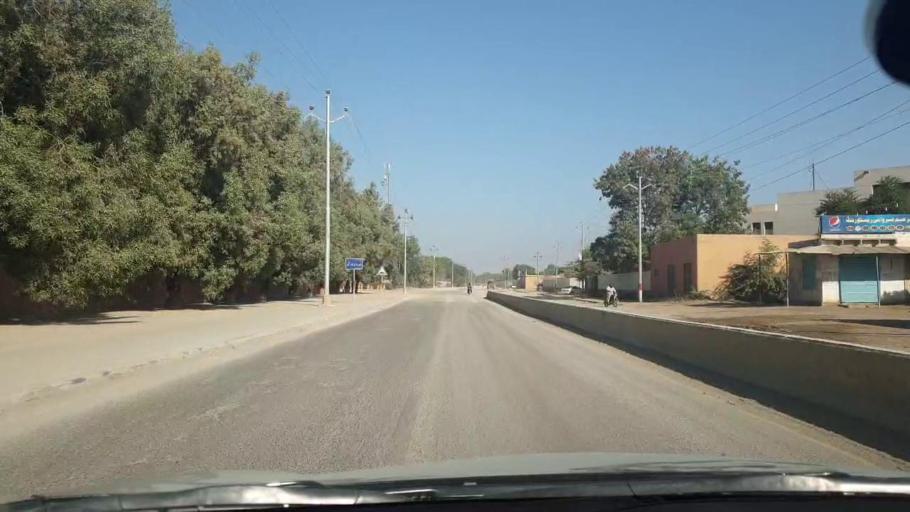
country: PK
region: Sindh
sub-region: Karachi District
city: Karachi
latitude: 25.0823
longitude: 67.0128
